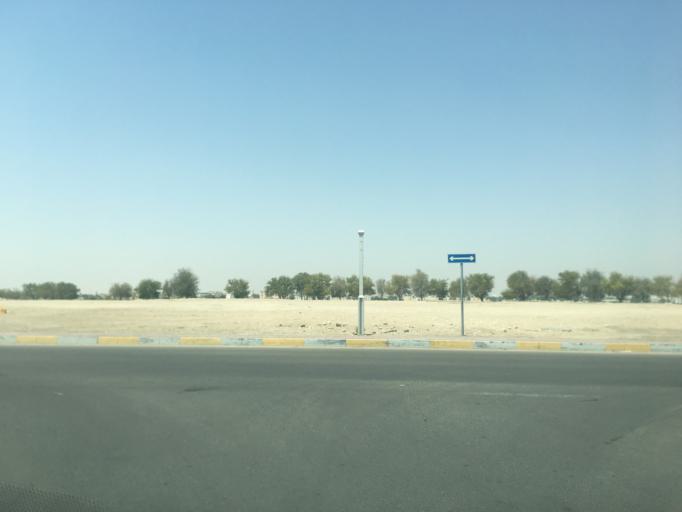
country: AE
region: Abu Dhabi
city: Abu Dhabi
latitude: 24.3079
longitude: 54.6347
